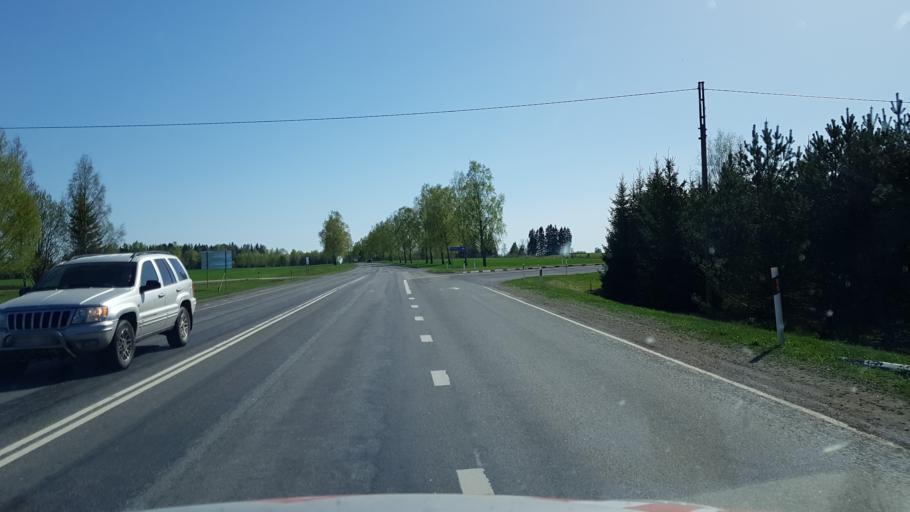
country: EE
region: Viljandimaa
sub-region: Viljandi linn
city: Viljandi
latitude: 58.3230
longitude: 25.5748
